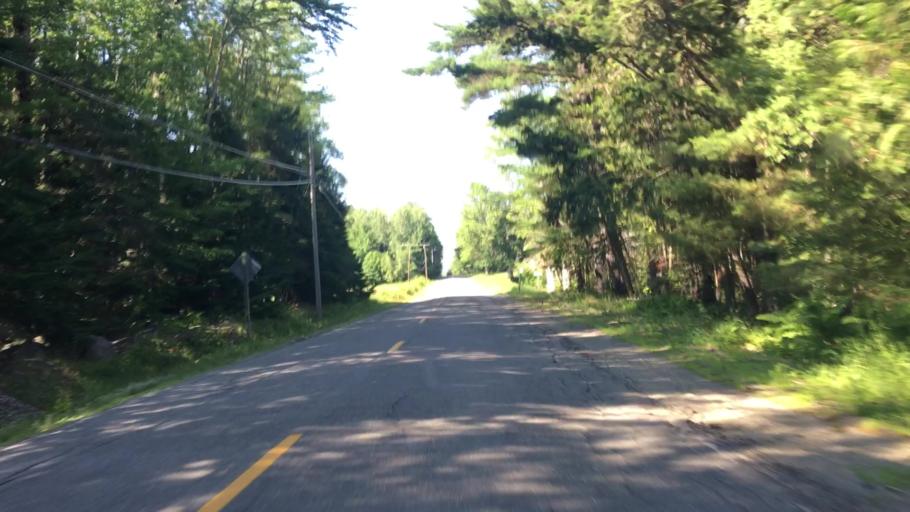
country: US
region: Maine
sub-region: Penobscot County
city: Enfield
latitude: 45.2609
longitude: -68.5630
